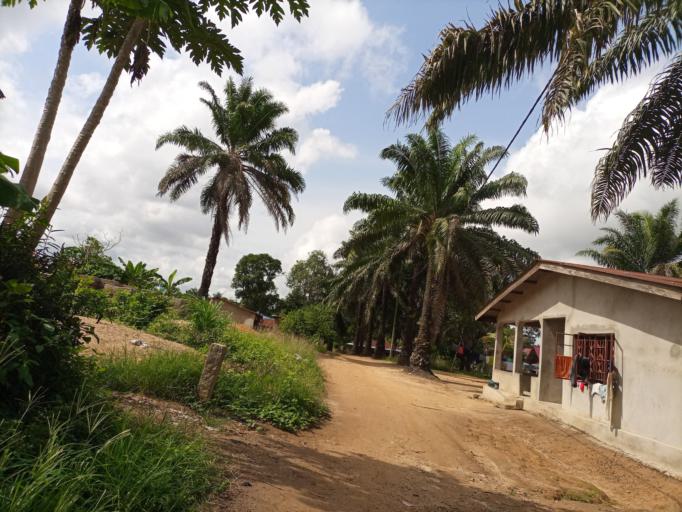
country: SL
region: Southern Province
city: Bo
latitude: 7.9602
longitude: -11.7613
